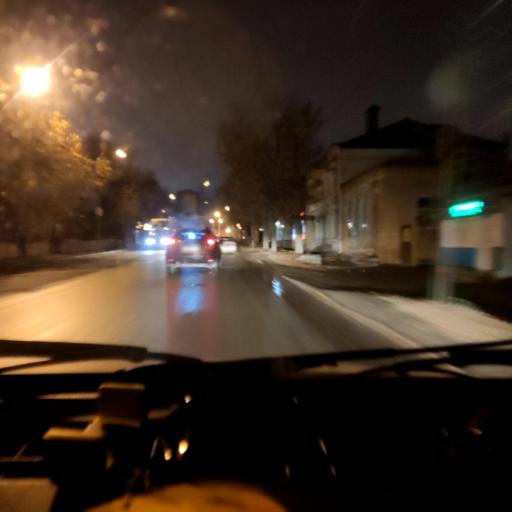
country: RU
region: Bashkortostan
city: Ufa
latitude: 54.7148
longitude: 55.9625
